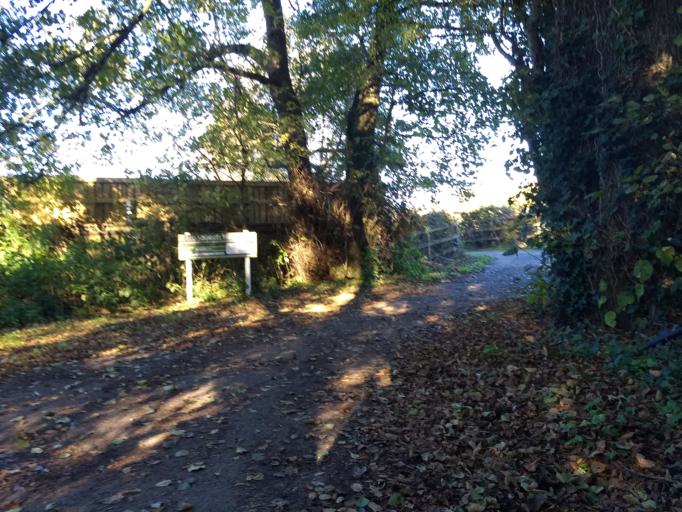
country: GB
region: England
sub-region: Isle of Wight
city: Newport
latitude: 50.6736
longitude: -1.2839
